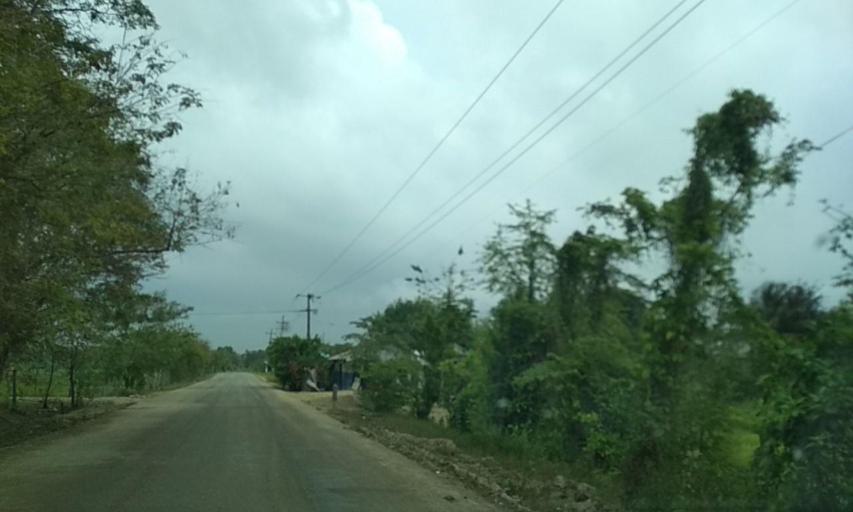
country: MX
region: Tabasco
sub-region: Huimanguillo
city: Francisco Rueda
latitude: 17.5893
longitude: -94.0920
